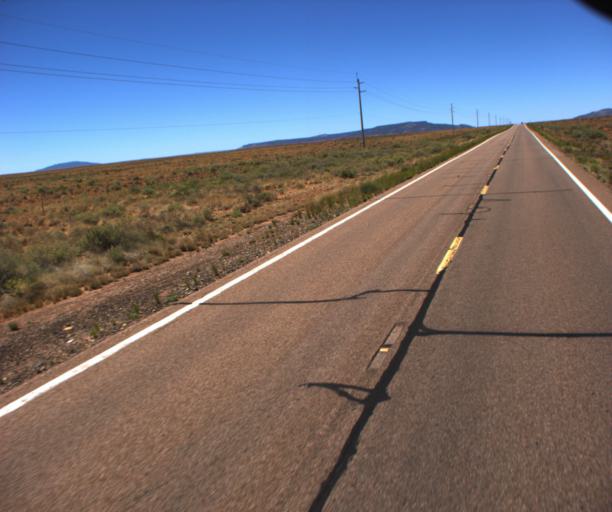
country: US
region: Arizona
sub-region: Coconino County
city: LeChee
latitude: 34.9501
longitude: -110.7630
